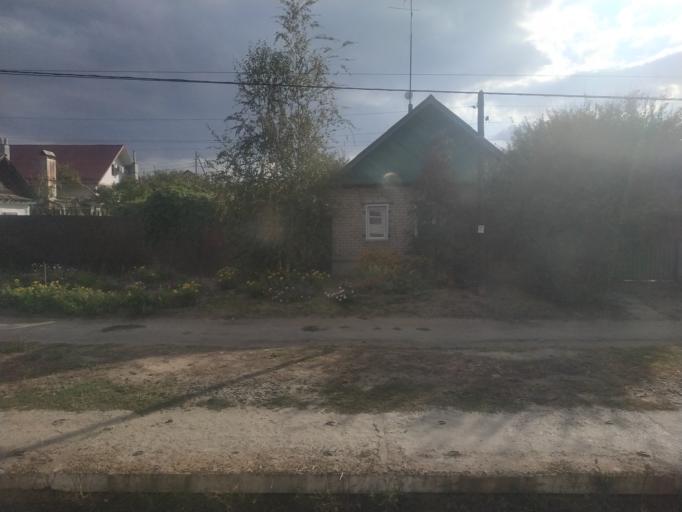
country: RU
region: Volgograd
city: Krasnoslobodsk
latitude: 48.5085
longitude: 44.5385
